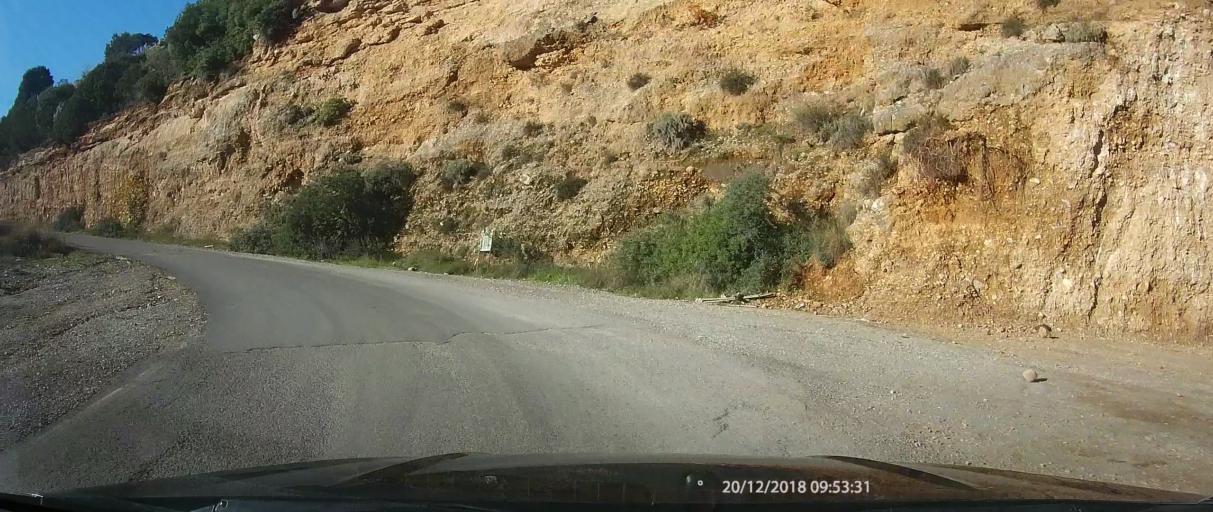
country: GR
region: Peloponnese
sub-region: Nomos Lakonias
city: Yerakion
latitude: 37.0123
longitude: 22.6384
